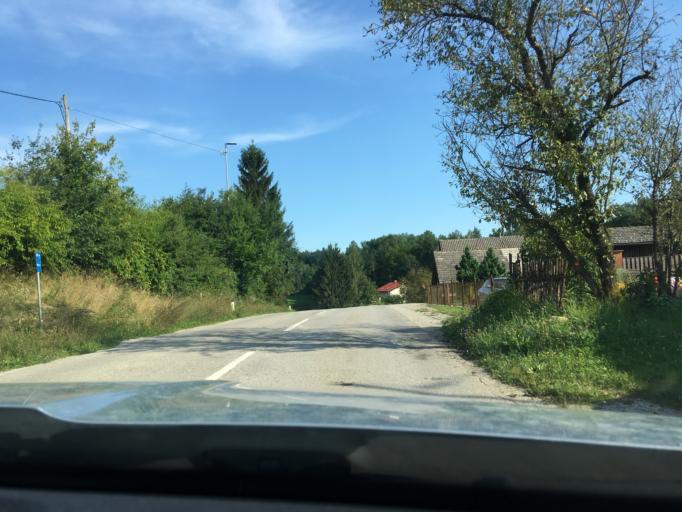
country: SI
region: Metlika
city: Metlika
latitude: 45.6135
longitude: 15.2504
